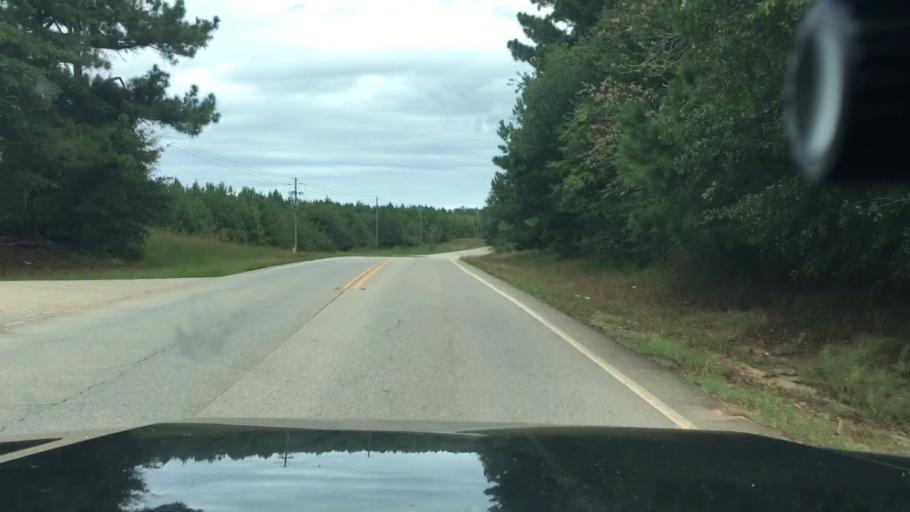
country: US
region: Georgia
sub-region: Coweta County
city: Grantville
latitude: 33.1863
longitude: -84.7983
